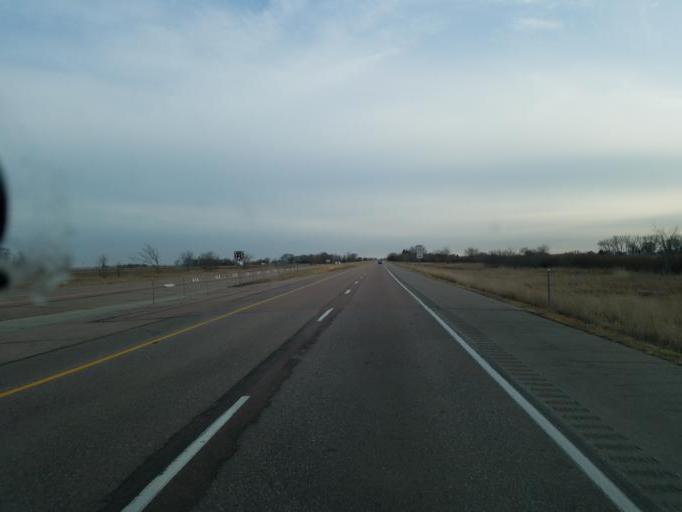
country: US
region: Iowa
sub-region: Monona County
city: Onawa
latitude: 42.1207
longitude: -96.2000
